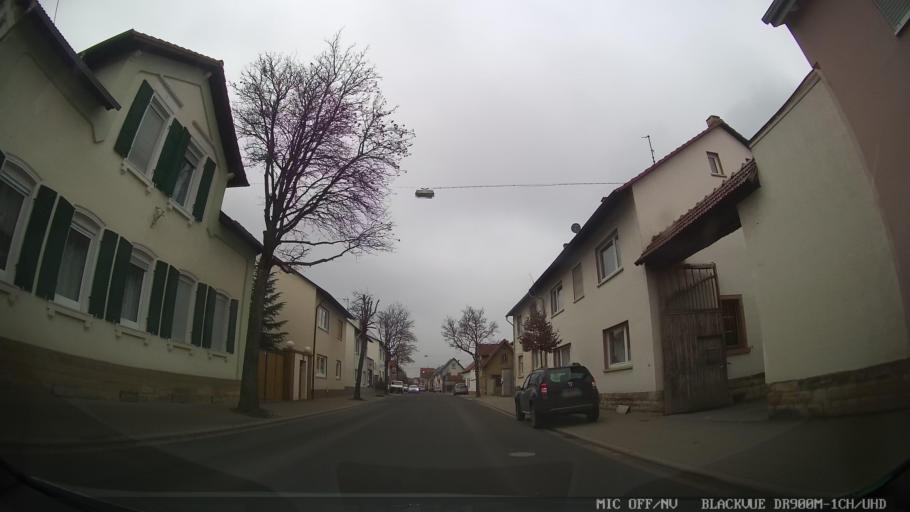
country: DE
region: Rheinland-Pfalz
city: Gau-Odernheim
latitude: 49.7811
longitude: 8.1972
